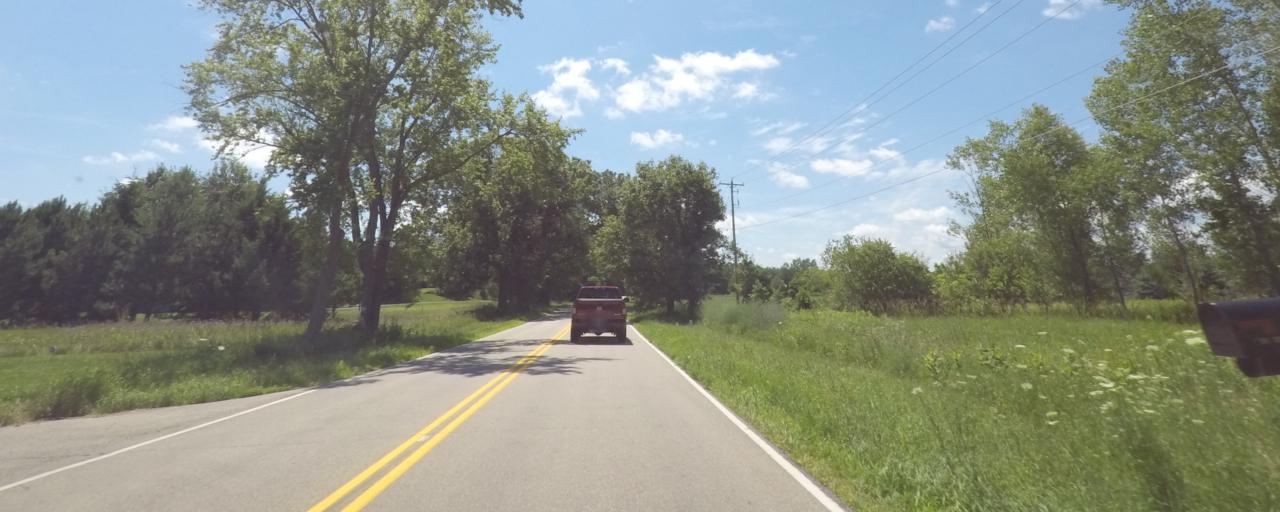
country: US
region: Wisconsin
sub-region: Waukesha County
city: Eagle
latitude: 42.9340
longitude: -88.5072
